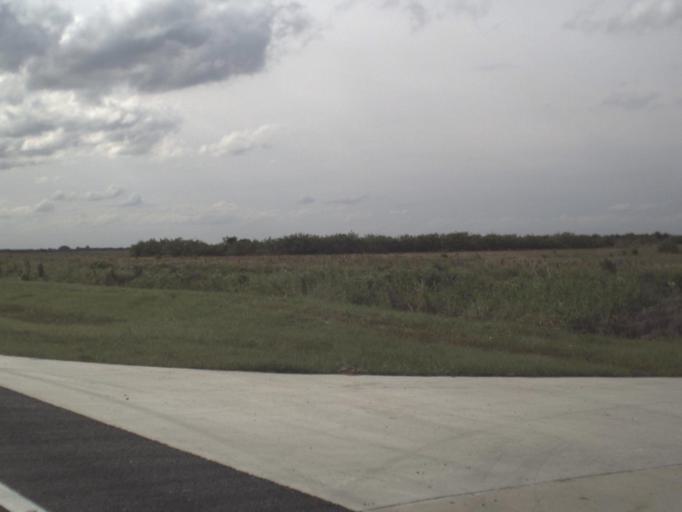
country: US
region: Florida
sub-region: Glades County
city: Moore Haven
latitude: 26.7534
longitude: -81.0989
